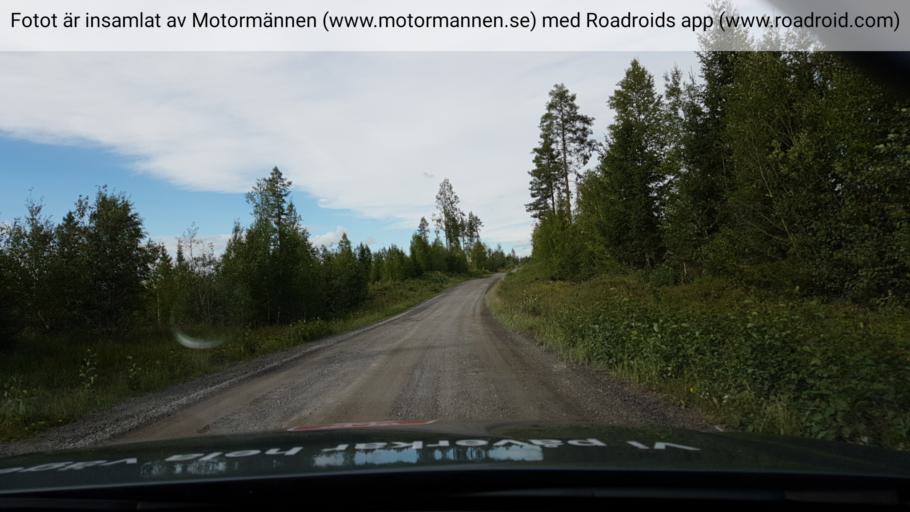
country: SE
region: Jaemtland
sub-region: Braecke Kommun
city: Braecke
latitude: 63.2447
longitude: 15.3689
